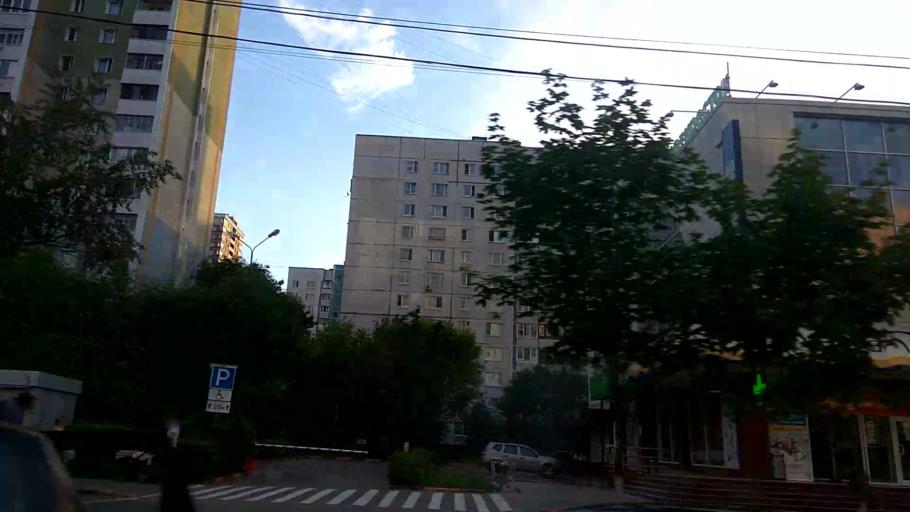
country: RU
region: Moskovskaya
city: Yubileyny
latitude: 55.9167
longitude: 37.8677
